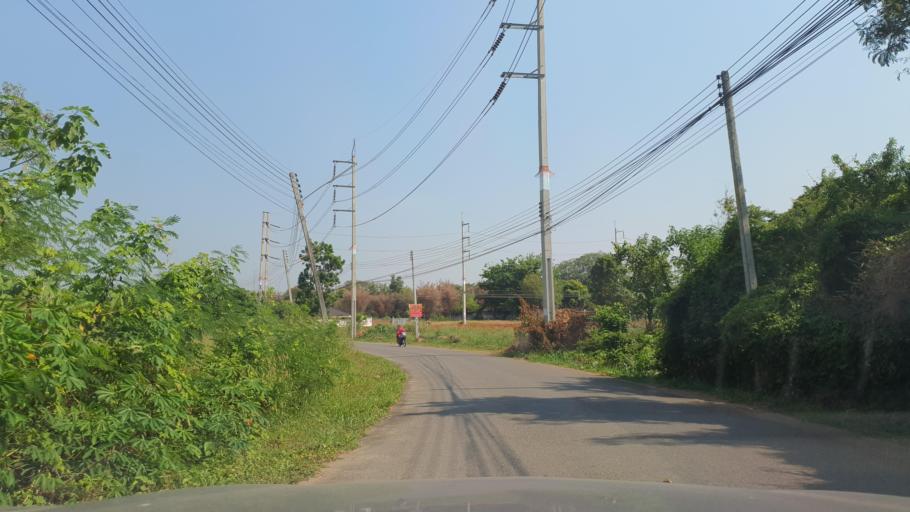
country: TH
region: Kanchanaburi
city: Kanchanaburi
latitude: 14.0677
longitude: 99.4860
